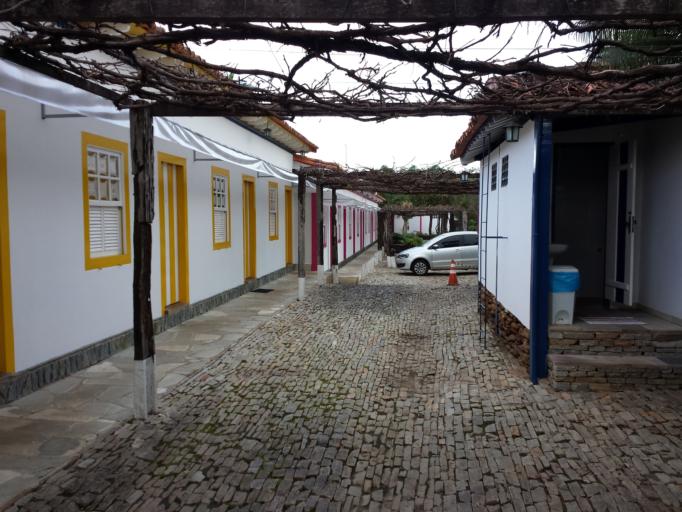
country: BR
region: Goias
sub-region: Pirenopolis
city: Pirenopolis
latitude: -15.8499
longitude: -48.9576
